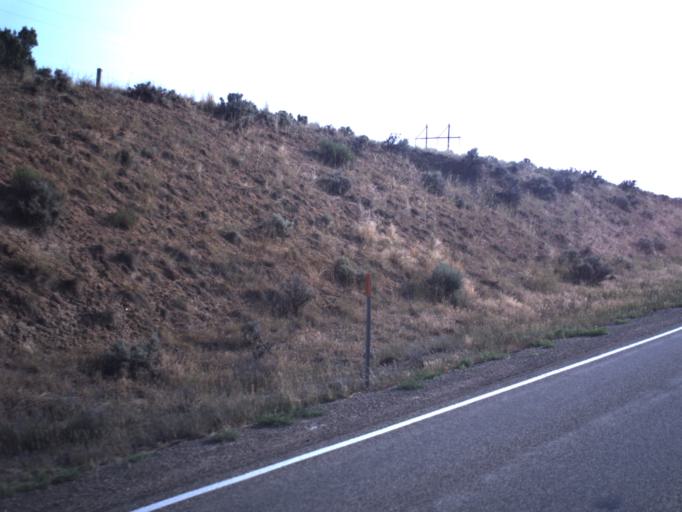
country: US
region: Utah
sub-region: Uintah County
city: Vernal
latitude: 40.5739
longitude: -109.4816
